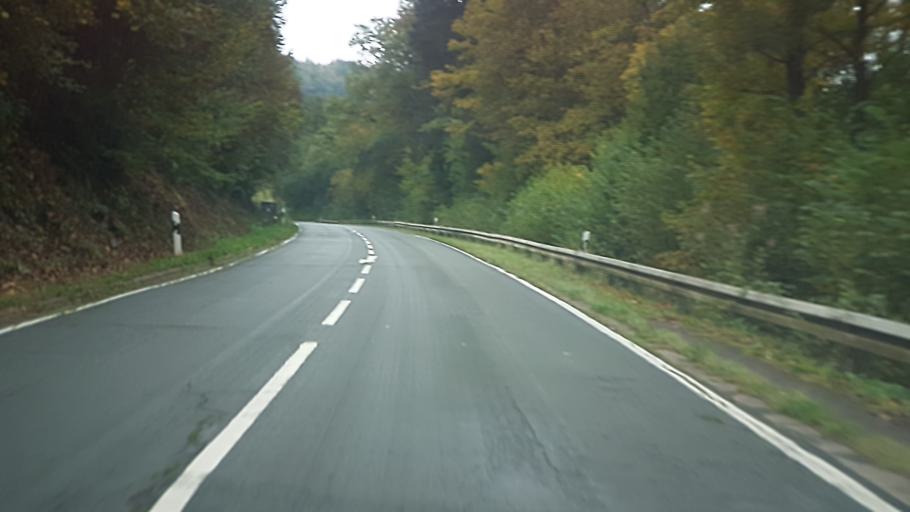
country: DE
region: North Rhine-Westphalia
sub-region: Regierungsbezirk Arnsberg
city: Herscheid
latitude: 51.2064
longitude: 7.6943
